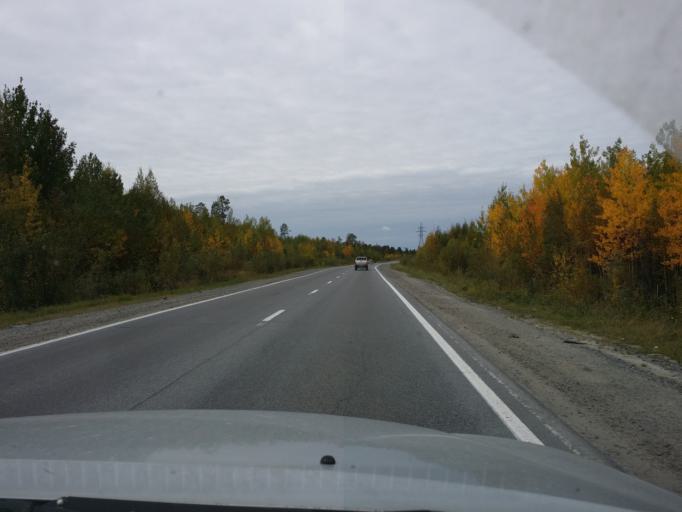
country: RU
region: Khanty-Mansiyskiy Avtonomnyy Okrug
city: Megion
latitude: 61.1029
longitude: 75.8875
